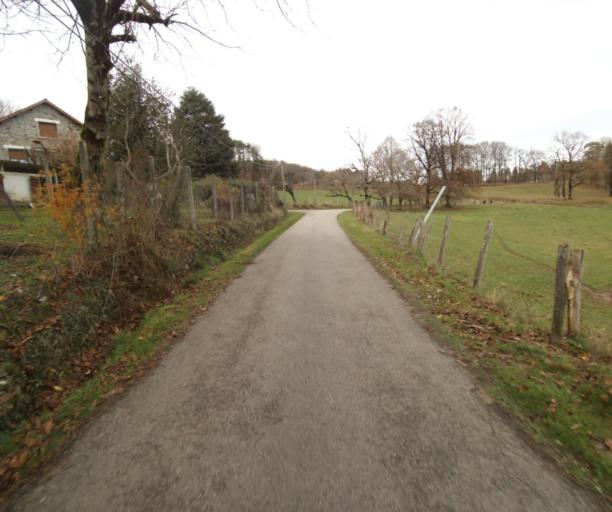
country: FR
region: Limousin
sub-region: Departement de la Correze
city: Saint-Mexant
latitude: 45.2549
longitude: 1.6601
